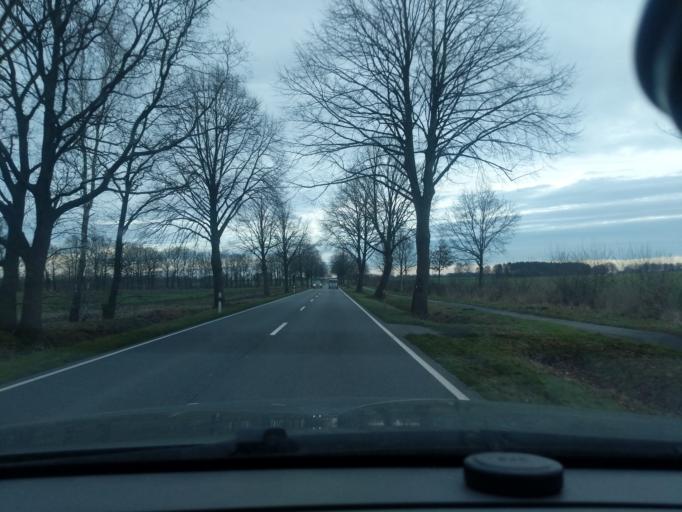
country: DE
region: Lower Saxony
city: Sauensiek
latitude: 53.3934
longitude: 9.6066
